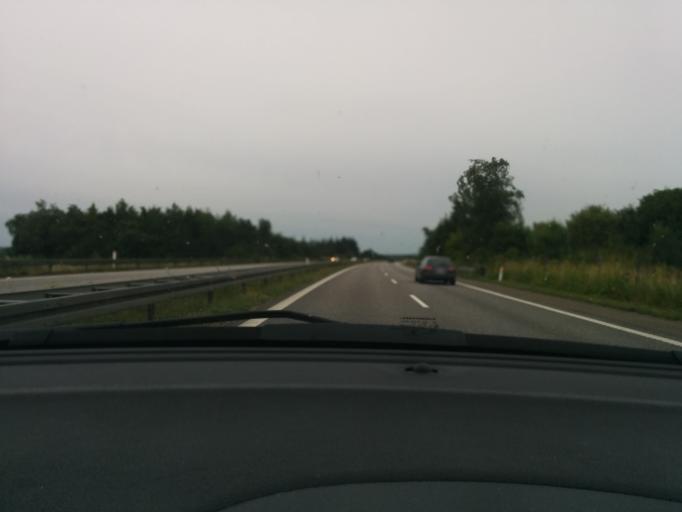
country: DK
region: Zealand
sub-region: Faxe Kommune
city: Ronnede
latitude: 55.1925
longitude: 11.9724
